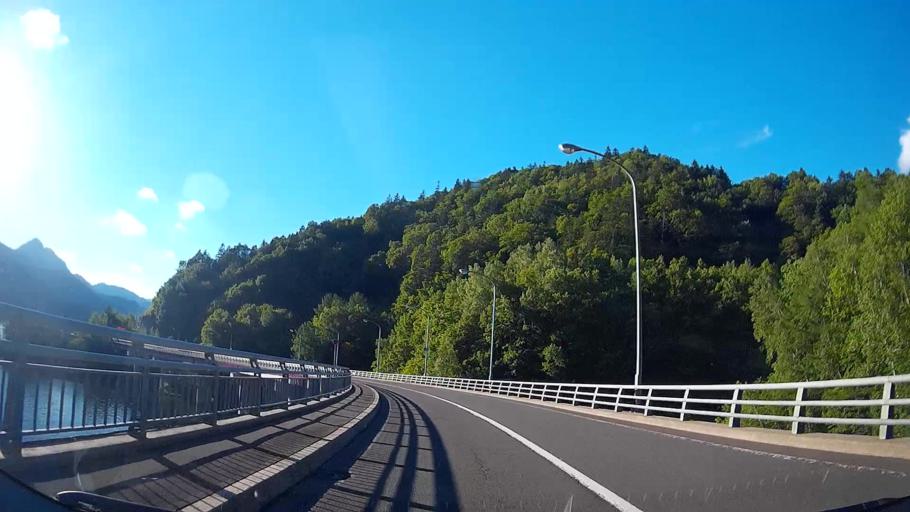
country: JP
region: Hokkaido
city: Sapporo
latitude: 42.9898
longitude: 141.1636
